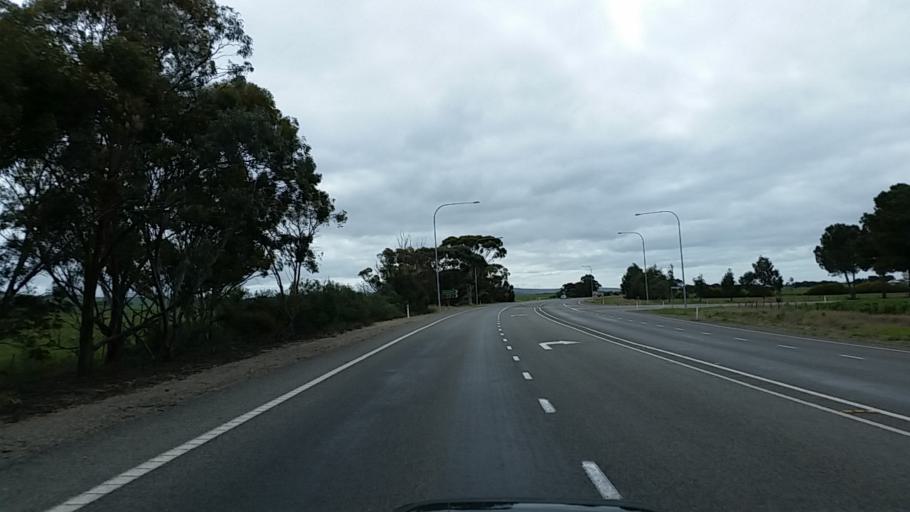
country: AU
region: South Australia
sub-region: Clare and Gilbert Valleys
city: Clare
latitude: -33.7885
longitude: 138.2071
